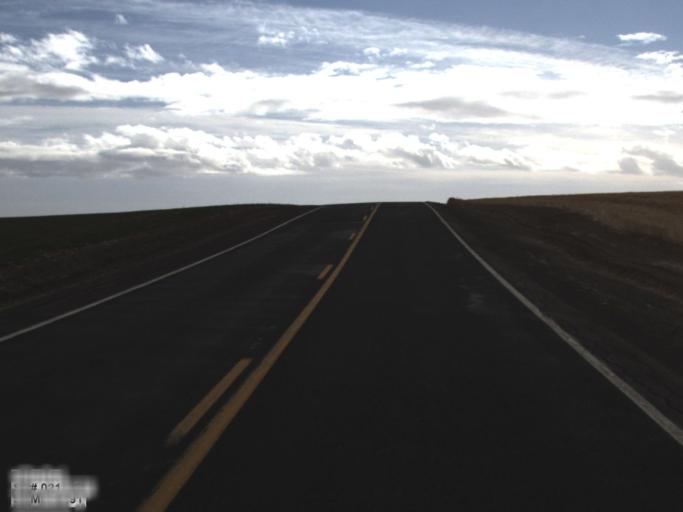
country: US
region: Washington
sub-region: Okanogan County
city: Coulee Dam
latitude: 47.7401
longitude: -118.7218
